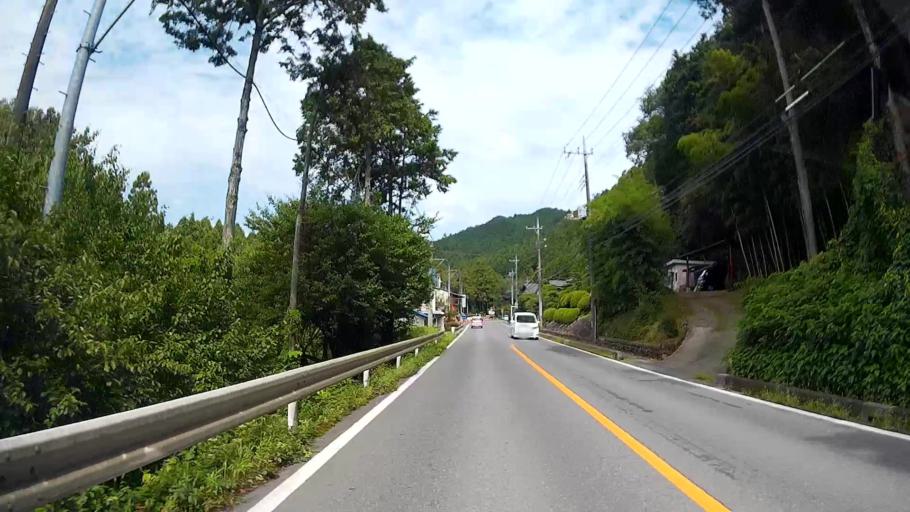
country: JP
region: Saitama
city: Hanno
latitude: 35.8673
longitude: 139.2833
